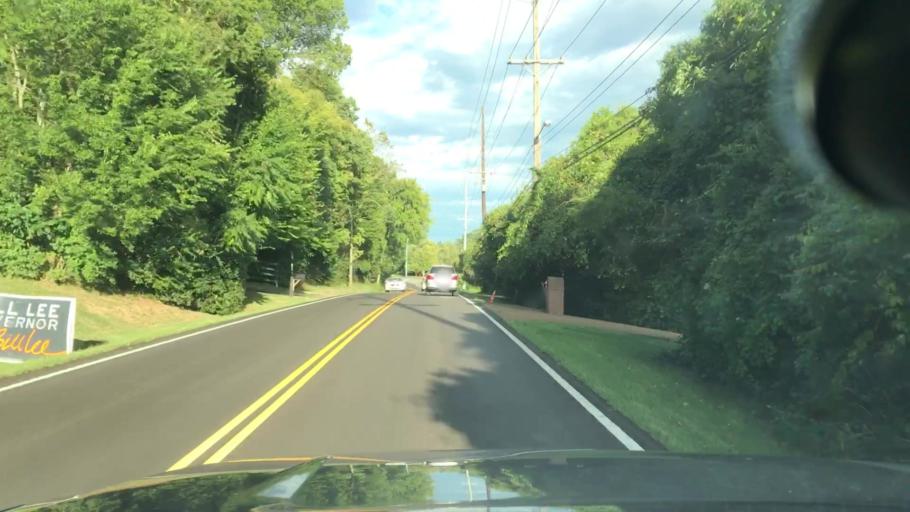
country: US
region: Tennessee
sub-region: Davidson County
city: Forest Hills
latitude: 36.0422
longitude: -86.8362
